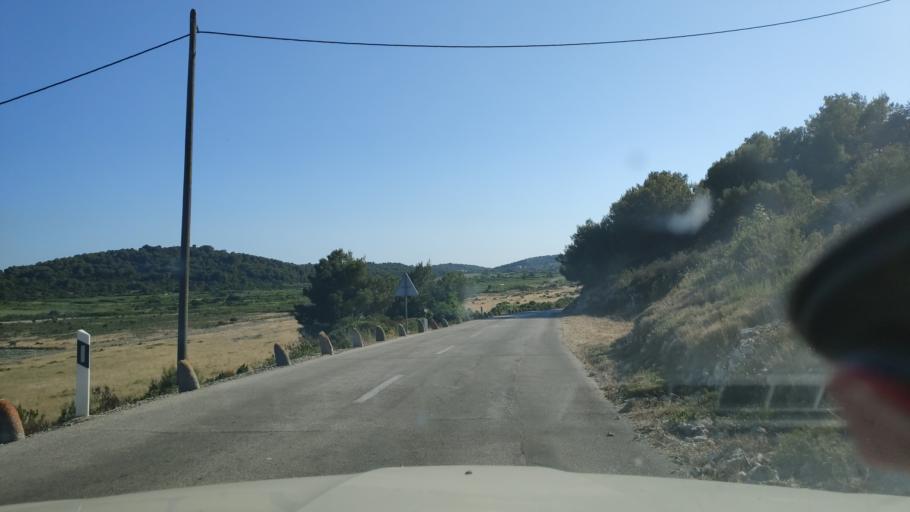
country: HR
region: Splitsko-Dalmatinska
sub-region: Grad Vis
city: Vis
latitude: 43.0438
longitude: 16.1978
